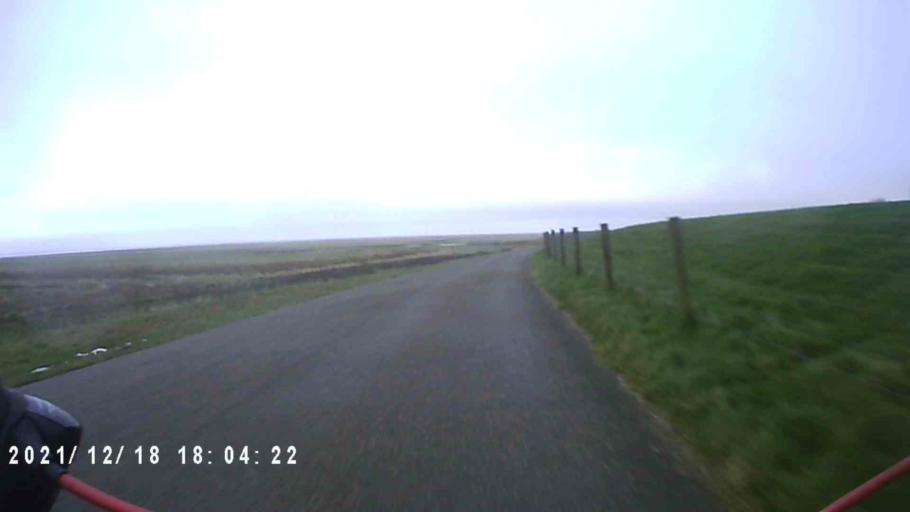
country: NL
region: Friesland
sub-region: Gemeente Dongeradeel
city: Holwerd
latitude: 53.3824
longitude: 5.9017
